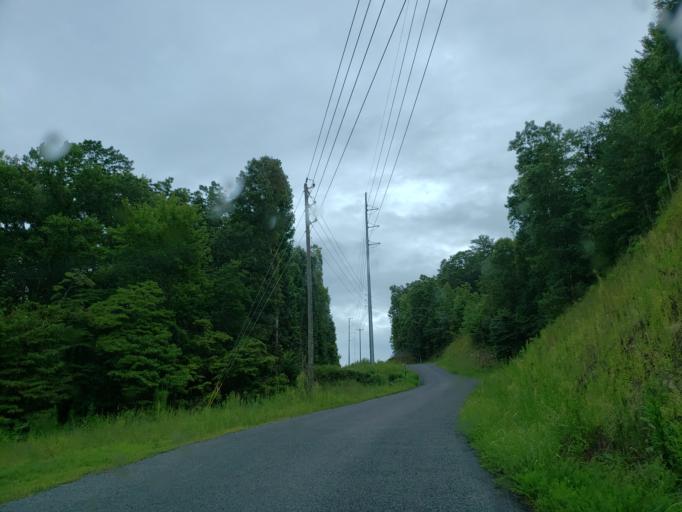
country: US
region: Georgia
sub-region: Gilmer County
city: Ellijay
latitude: 34.6188
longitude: -84.5756
